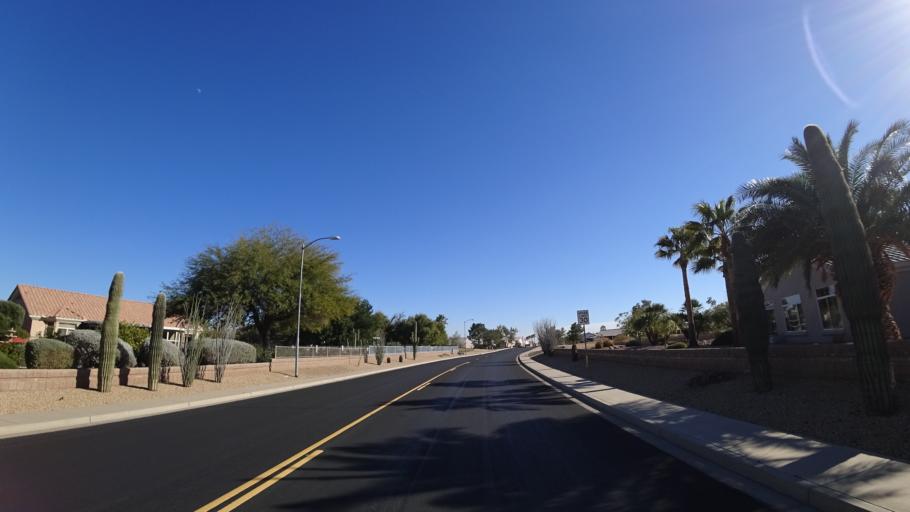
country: US
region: Arizona
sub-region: Maricopa County
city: Sun City West
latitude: 33.6926
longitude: -112.3698
